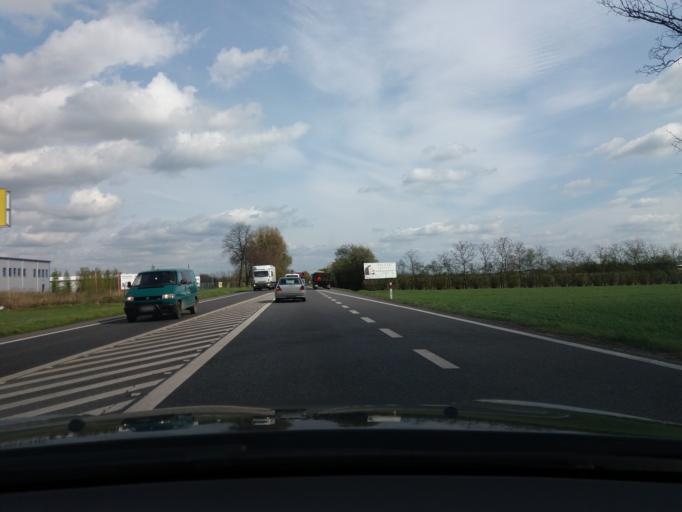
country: PL
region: Lower Silesian Voivodeship
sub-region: Powiat sredzki
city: Mrozow
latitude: 51.1575
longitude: 16.7950
